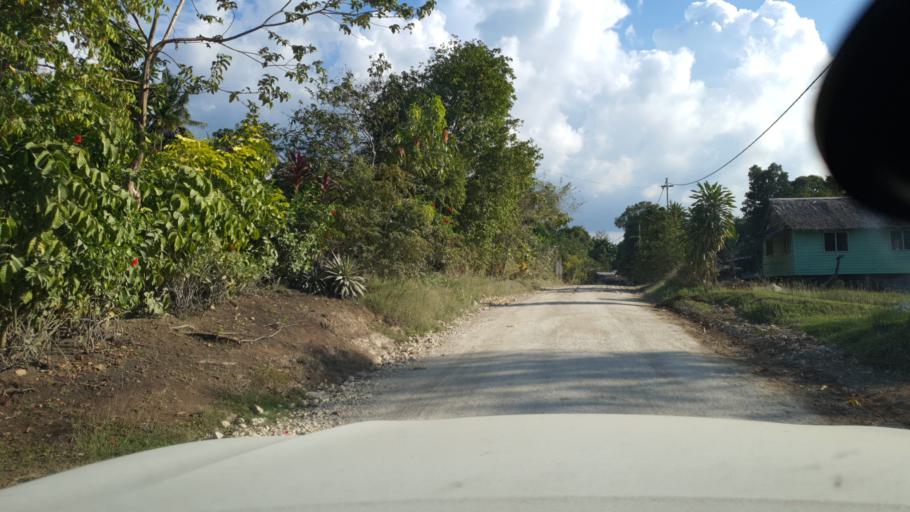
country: SB
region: Guadalcanal
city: Honiara
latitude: -9.4498
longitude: 159.9945
